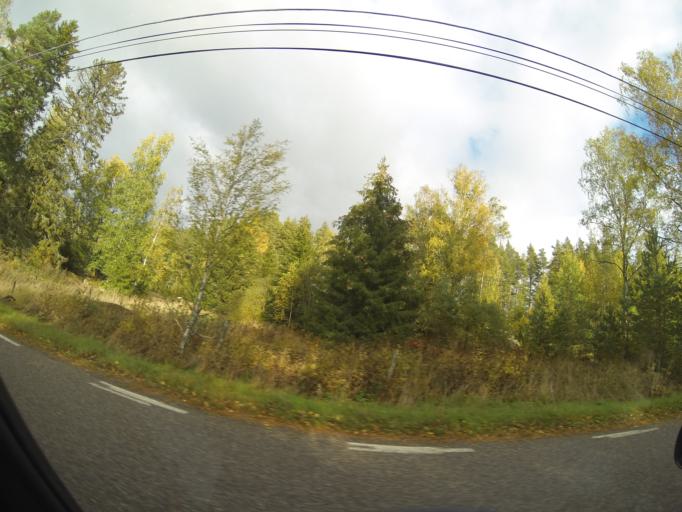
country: SE
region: Soedermanland
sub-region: Eskilstuna Kommun
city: Kvicksund
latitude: 59.3199
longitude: 16.2681
